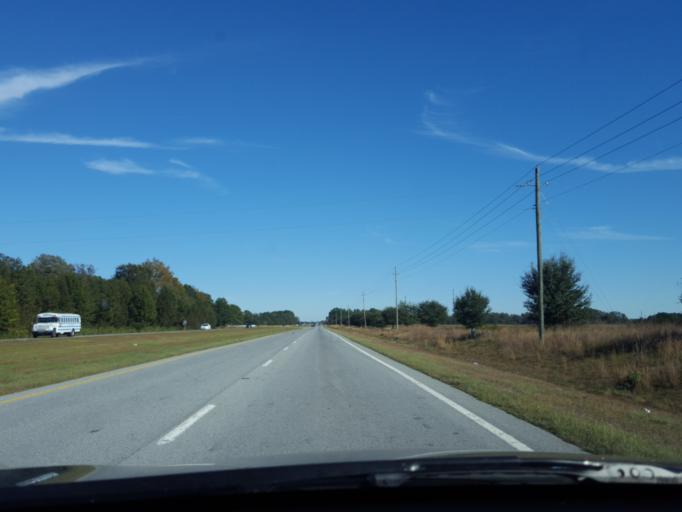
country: US
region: North Carolina
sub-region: Pitt County
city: Greenville
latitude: 35.6256
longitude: -77.2966
